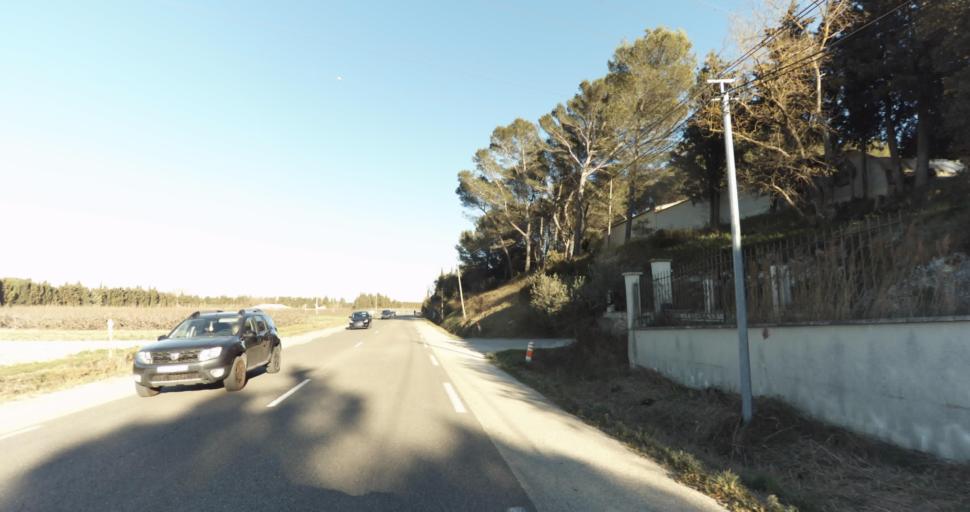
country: FR
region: Provence-Alpes-Cote d'Azur
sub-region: Departement des Bouches-du-Rhone
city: Barbentane
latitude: 43.8975
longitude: 4.7184
